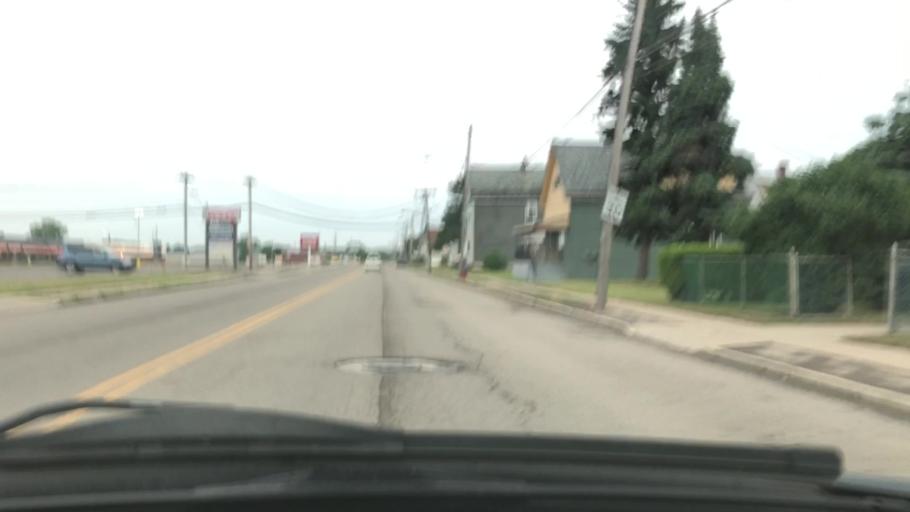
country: US
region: New York
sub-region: Erie County
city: Sloan
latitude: 42.8785
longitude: -78.8012
